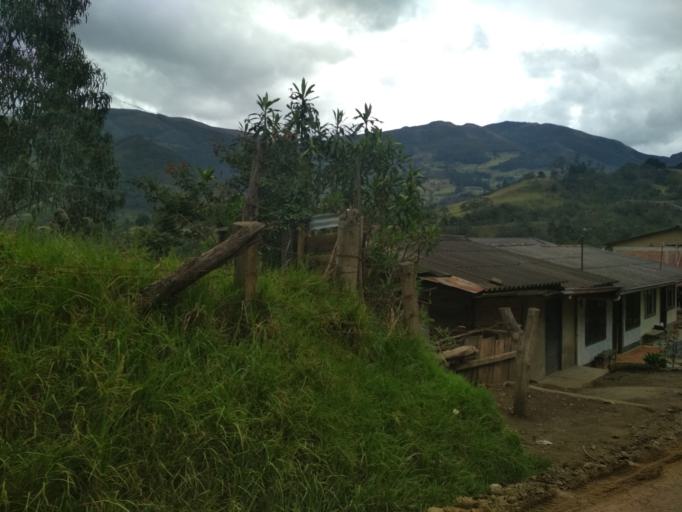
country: CO
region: Cauca
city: Jambalo
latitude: 2.7125
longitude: -76.3255
